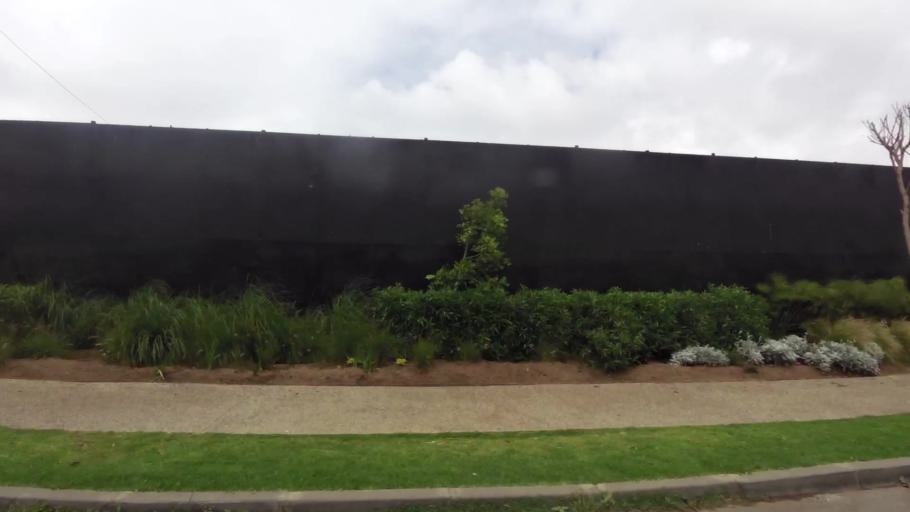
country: MA
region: Grand Casablanca
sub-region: Casablanca
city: Casablanca
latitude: 33.6007
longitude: -7.6508
